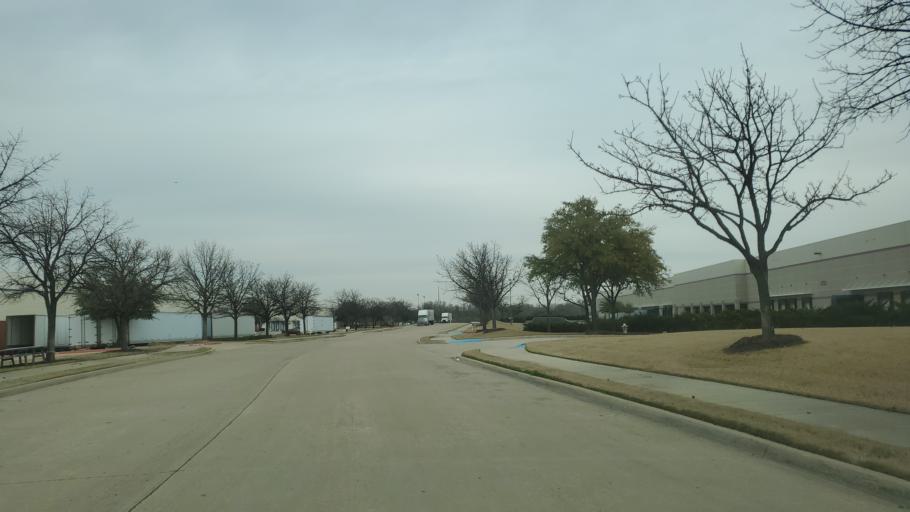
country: US
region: Texas
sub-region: Dallas County
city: Coppell
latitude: 32.9857
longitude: -97.0238
